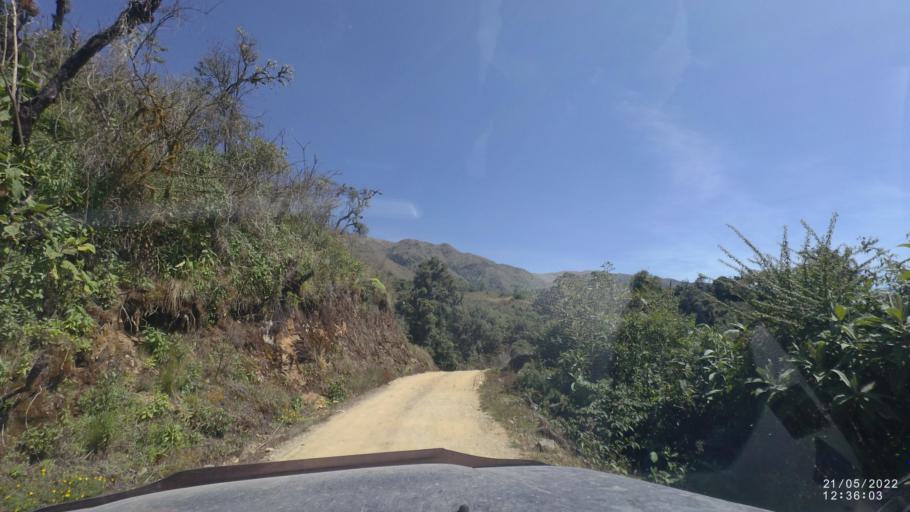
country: BO
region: Cochabamba
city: Colomi
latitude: -17.2042
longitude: -65.9168
